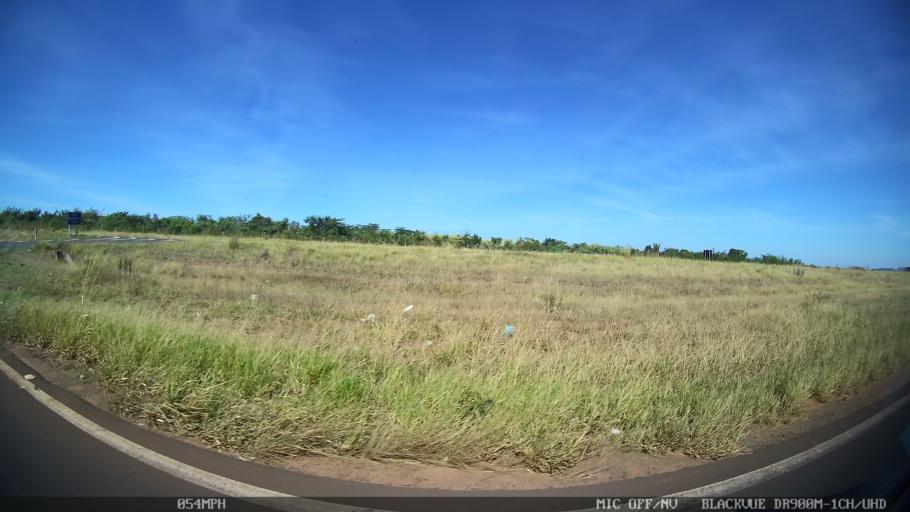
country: BR
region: Sao Paulo
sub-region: Franca
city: Franca
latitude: -20.5466
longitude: -47.4775
